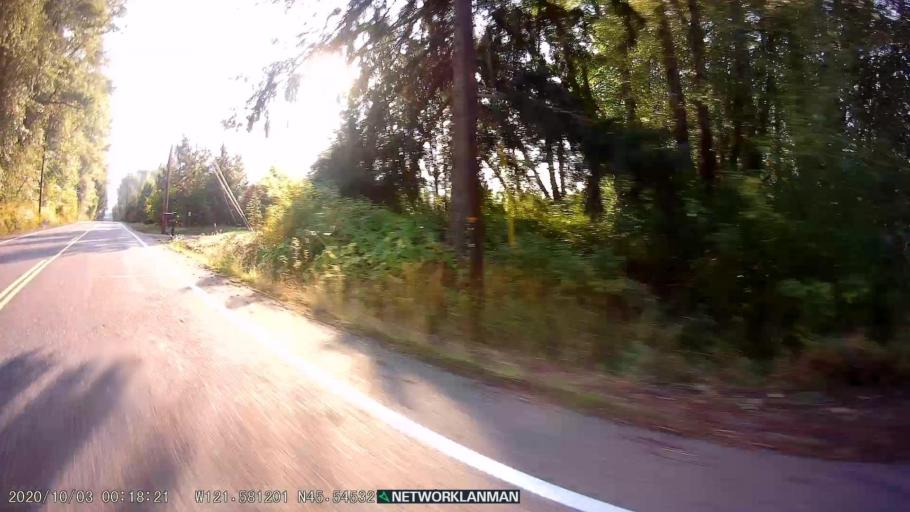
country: US
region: Oregon
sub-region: Hood River County
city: Odell
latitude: 45.5453
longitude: -121.5808
